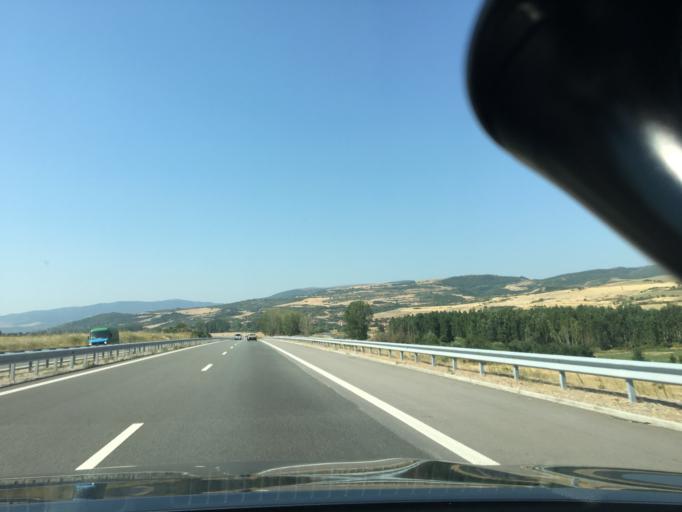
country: BG
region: Kyustendil
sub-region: Obshtina Dupnitsa
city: Dupnitsa
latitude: 42.2126
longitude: 23.0685
